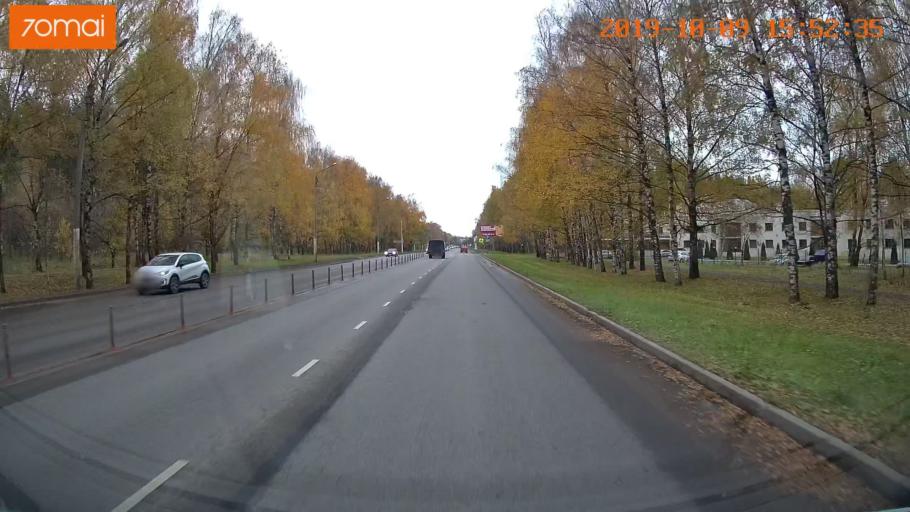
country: RU
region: Kostroma
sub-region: Kostromskoy Rayon
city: Kostroma
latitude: 57.7885
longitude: 40.9662
